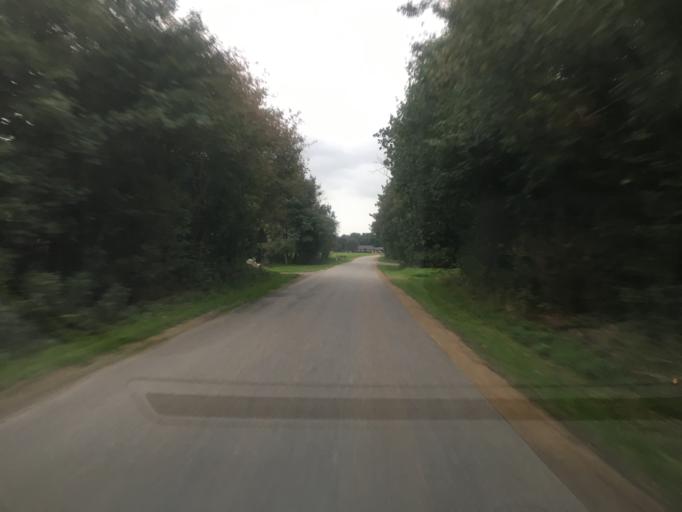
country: DK
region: South Denmark
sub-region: Tonder Kommune
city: Logumkloster
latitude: 55.0011
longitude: 9.0169
